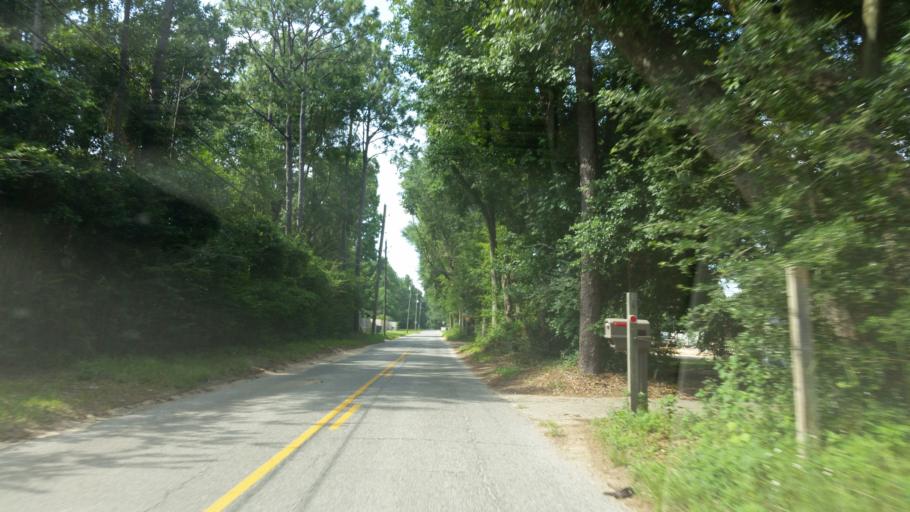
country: US
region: Florida
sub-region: Escambia County
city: Cantonment
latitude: 30.5702
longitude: -87.3624
